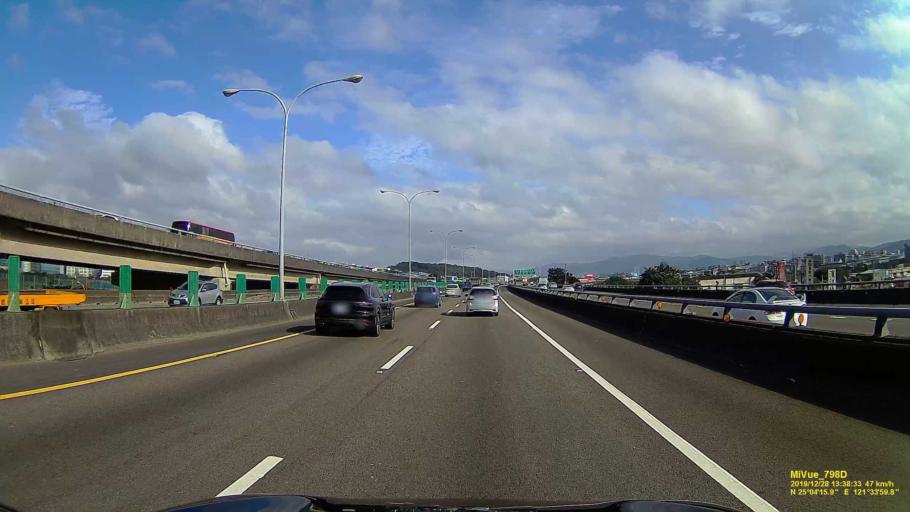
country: TW
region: Taipei
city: Taipei
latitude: 25.0714
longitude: 121.5677
